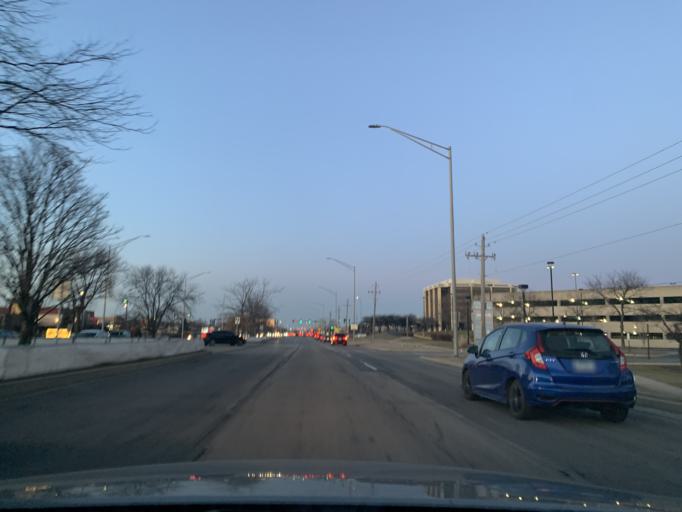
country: US
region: Illinois
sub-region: Cook County
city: Hoffman Estates
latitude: 42.0457
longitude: -88.0452
